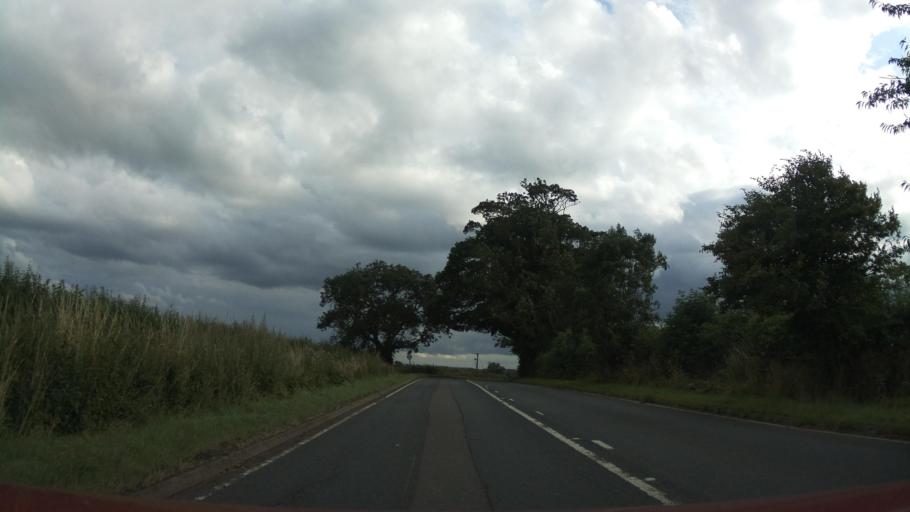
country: GB
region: England
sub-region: Warwickshire
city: Dunchurch
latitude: 52.3282
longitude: -1.2995
